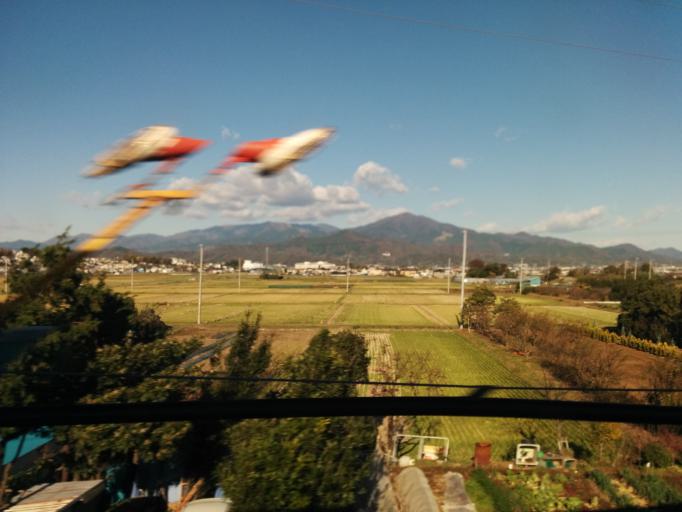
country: JP
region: Kanagawa
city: Hiratsuka
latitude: 35.3483
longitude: 139.3132
